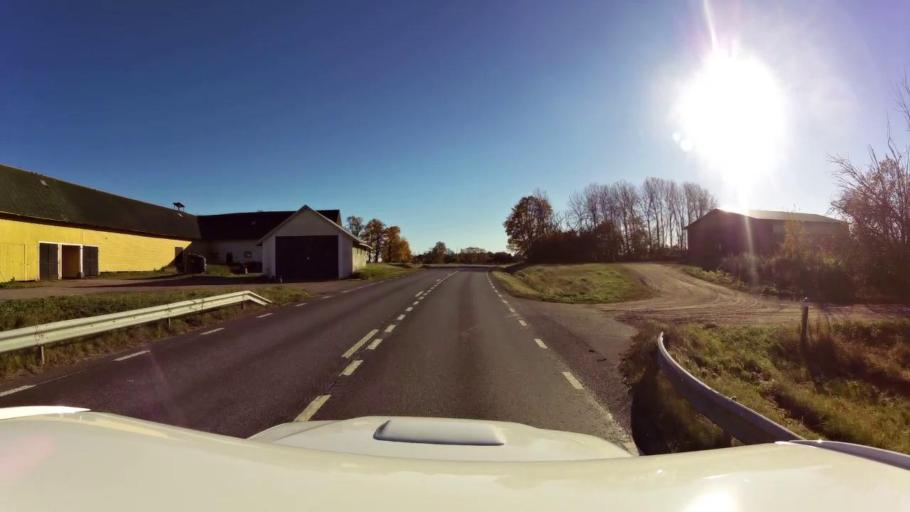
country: SE
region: OEstergoetland
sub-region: Linkopings Kommun
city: Ljungsbro
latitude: 58.5287
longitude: 15.4077
